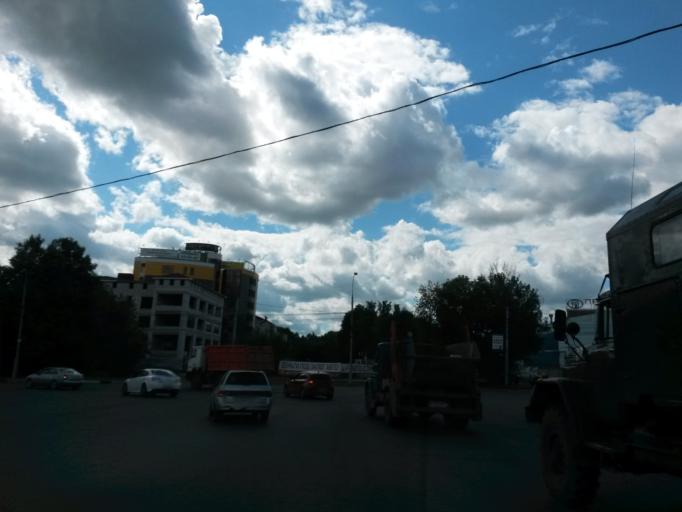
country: RU
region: Jaroslavl
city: Yaroslavl
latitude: 57.6089
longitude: 39.8602
